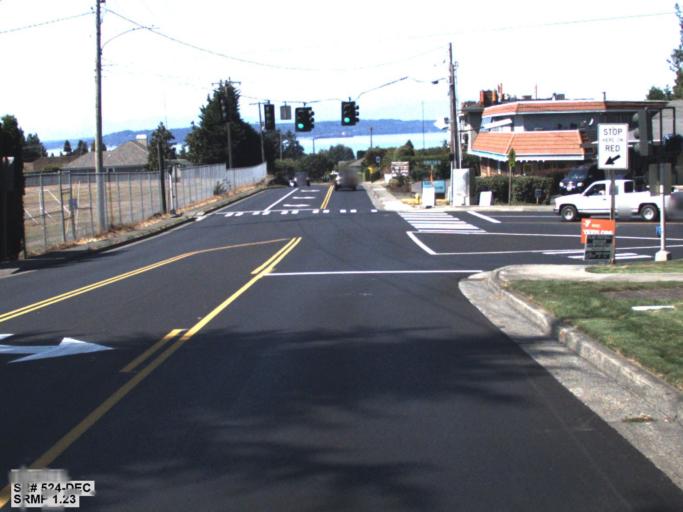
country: US
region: Washington
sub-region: Snohomish County
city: Edmonds
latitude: 47.8215
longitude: -122.3637
